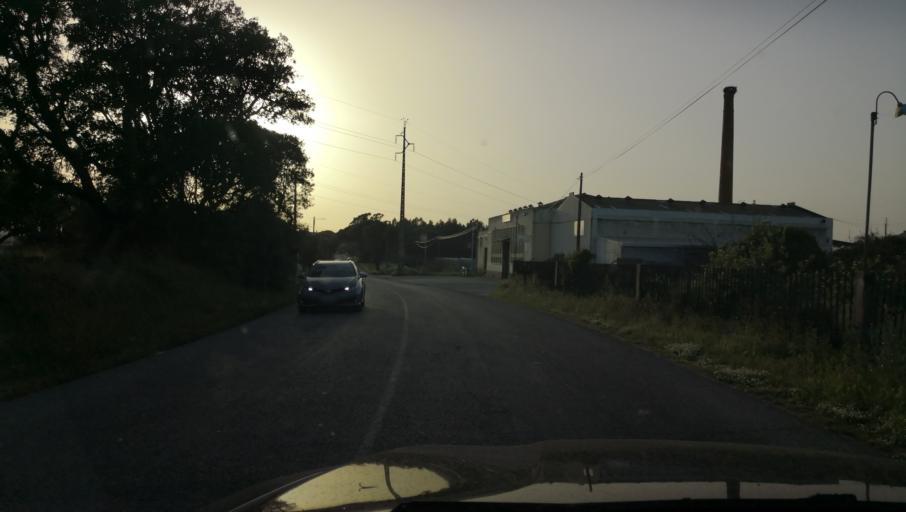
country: PT
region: Setubal
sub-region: Setubal
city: Setubal
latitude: 38.5383
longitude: -8.8295
